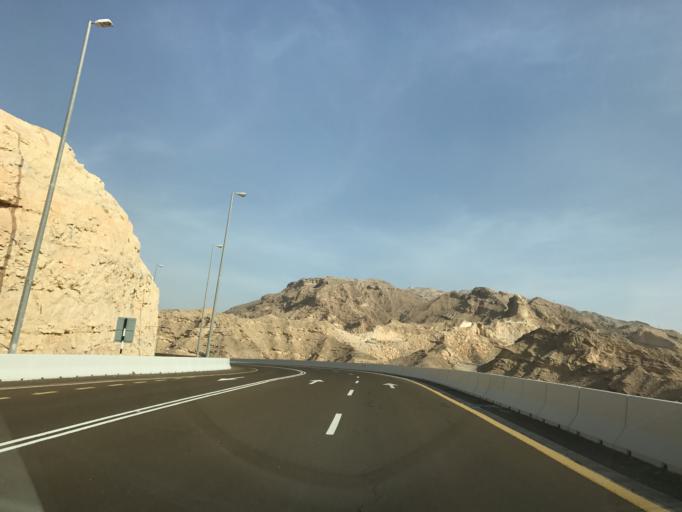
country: AE
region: Abu Dhabi
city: Al Ain
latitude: 24.1069
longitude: 55.7576
